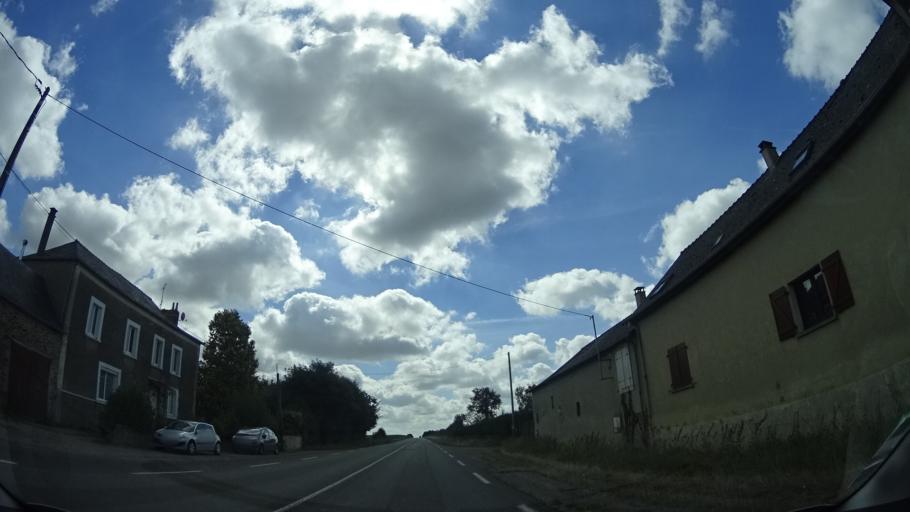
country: FR
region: Pays de la Loire
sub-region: Departement de la Mayenne
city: Entrammes
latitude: 47.9975
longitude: -0.6405
